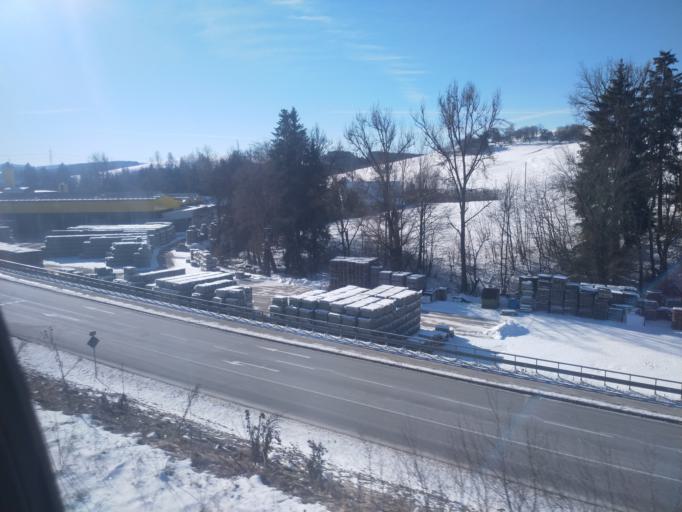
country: DE
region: Baden-Wuerttemberg
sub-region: Freiburg Region
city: Aldingen
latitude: 48.1153
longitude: 8.6918
